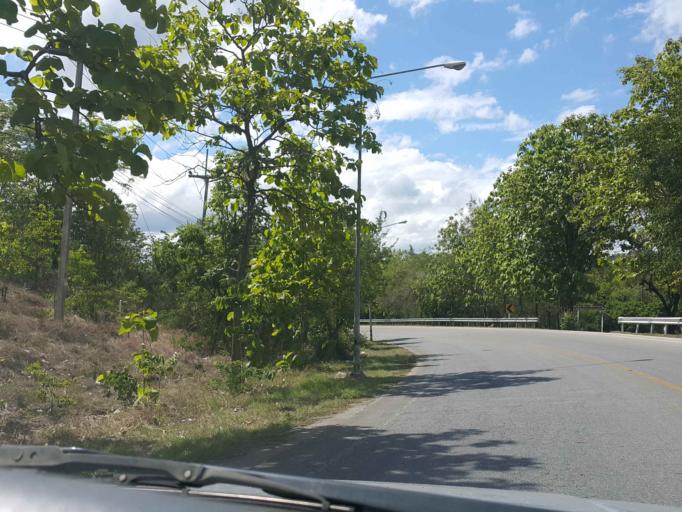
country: TH
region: Chiang Mai
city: Chom Thong
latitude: 18.4759
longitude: 98.6760
